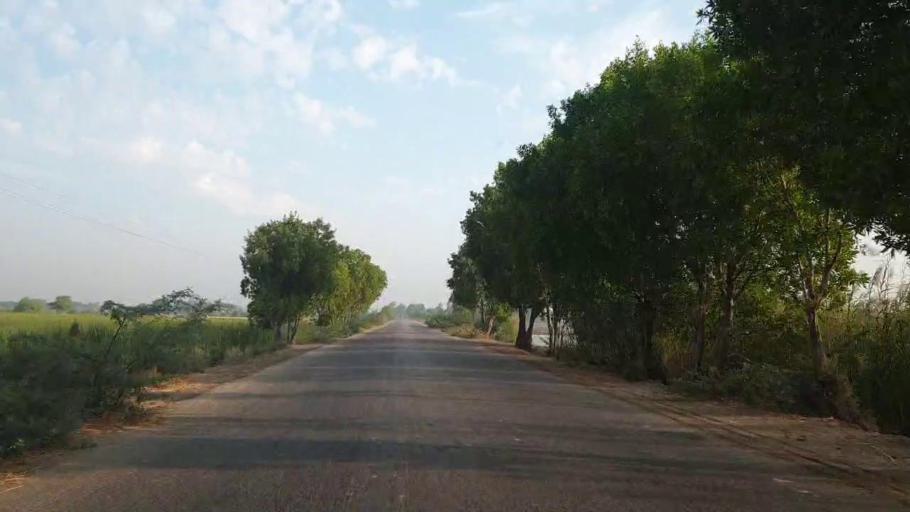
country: PK
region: Sindh
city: Tando Bago
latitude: 24.7367
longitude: 68.9458
